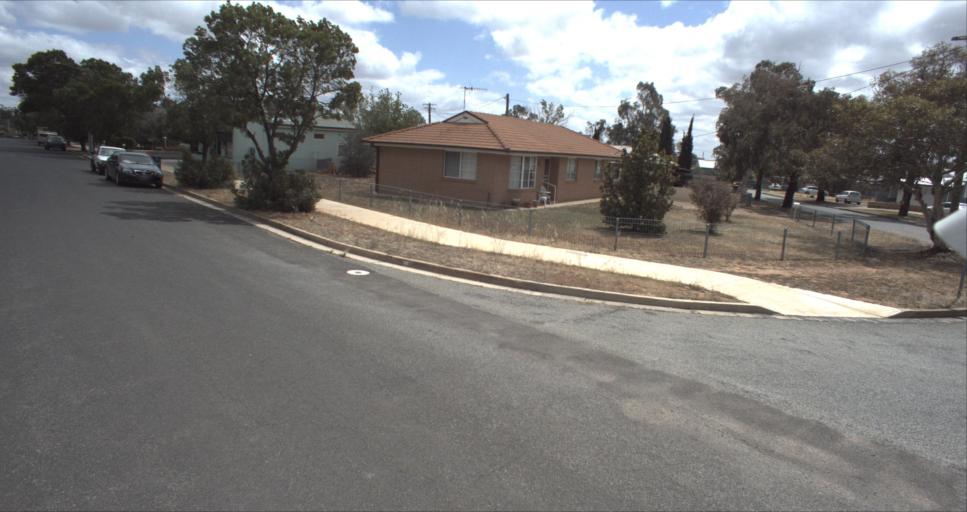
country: AU
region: New South Wales
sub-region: Leeton
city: Leeton
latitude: -34.5606
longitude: 146.3959
